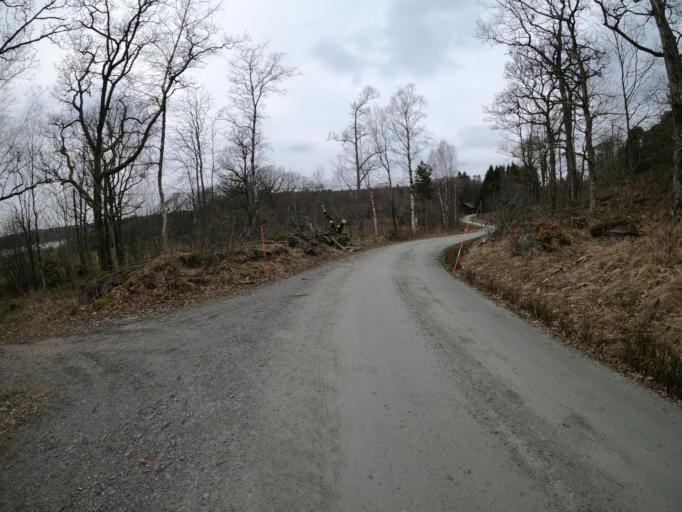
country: SE
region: Vaestra Goetaland
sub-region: Harryda Kommun
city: Molnlycke
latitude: 57.6297
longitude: 12.1062
